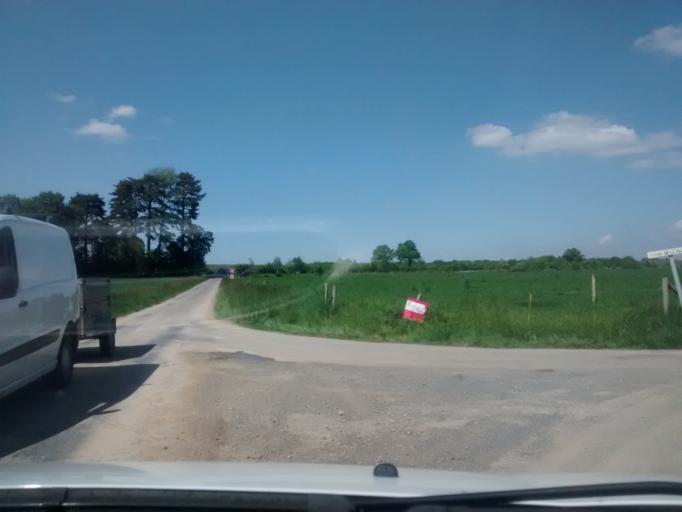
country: FR
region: Brittany
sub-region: Departement d'Ille-et-Vilaine
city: Fouillard
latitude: 48.1541
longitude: -1.6105
